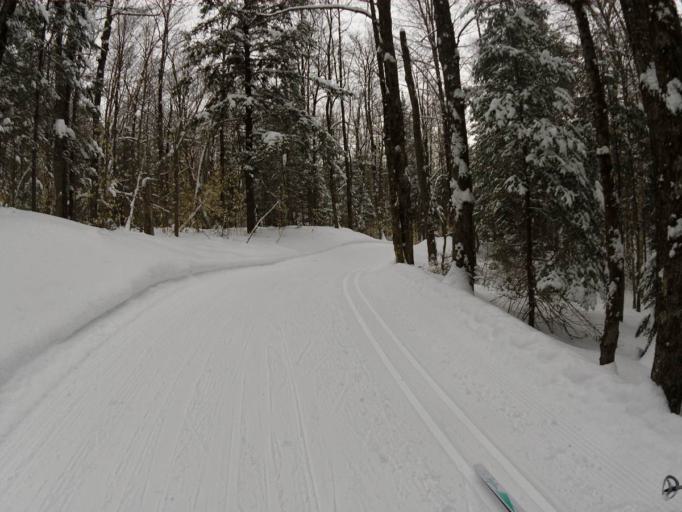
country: CA
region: Quebec
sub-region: Outaouais
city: Wakefield
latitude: 45.5939
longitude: -76.0114
